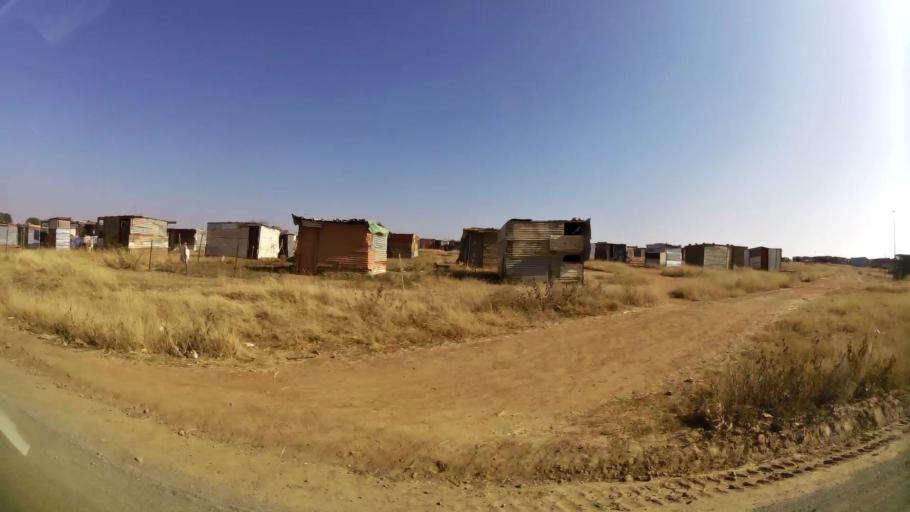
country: ZA
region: Orange Free State
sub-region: Mangaung Metropolitan Municipality
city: Bloemfontein
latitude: -29.1873
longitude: 26.2848
